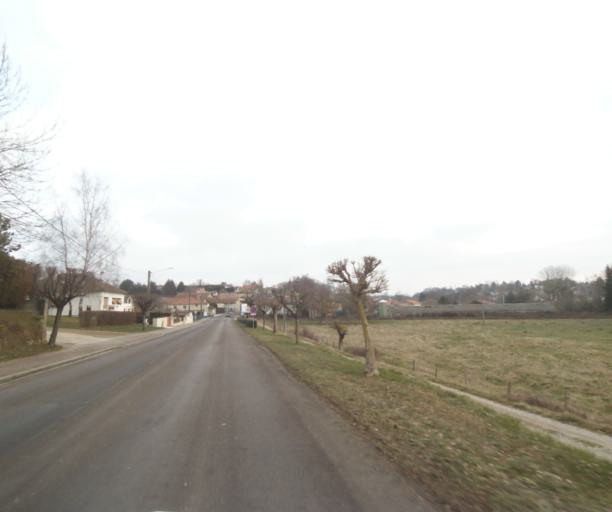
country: FR
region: Champagne-Ardenne
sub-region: Departement de la Haute-Marne
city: Chancenay
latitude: 48.6666
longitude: 4.9820
